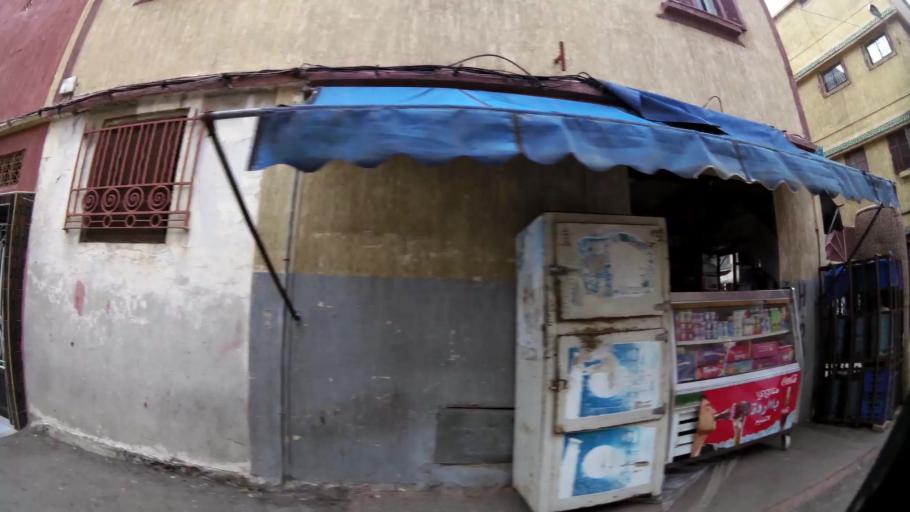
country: MA
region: Grand Casablanca
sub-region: Casablanca
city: Casablanca
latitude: 33.5845
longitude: -7.5593
